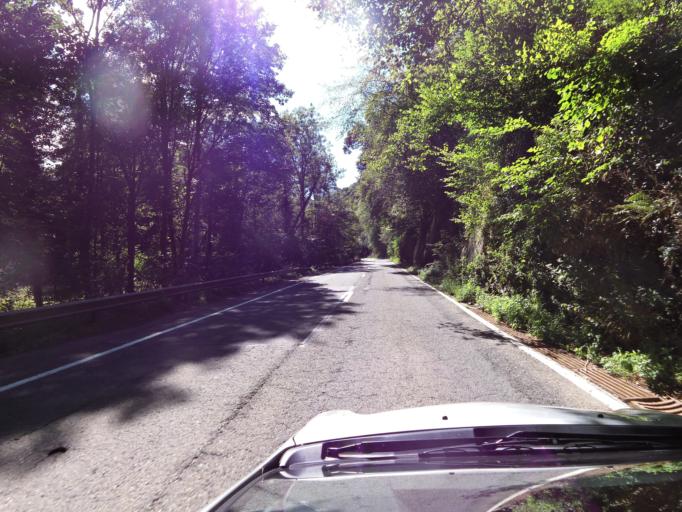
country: BE
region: Wallonia
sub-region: Province du Luxembourg
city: Rendeux
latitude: 50.2140
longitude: 5.5193
